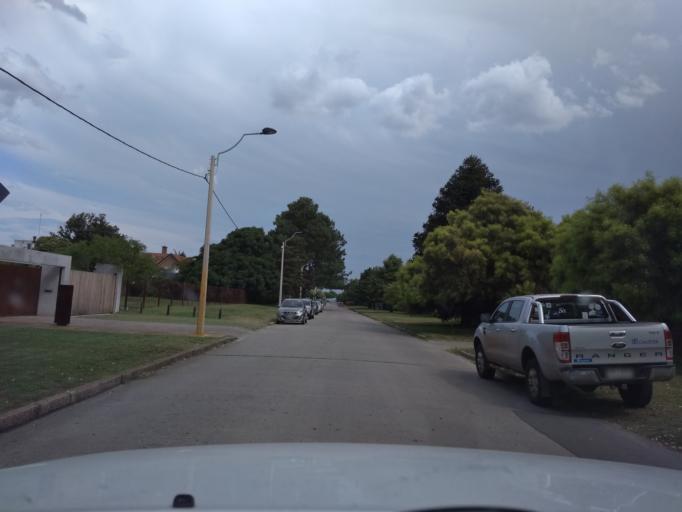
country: UY
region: Canelones
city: Barra de Carrasco
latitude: -34.8832
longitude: -56.0490
